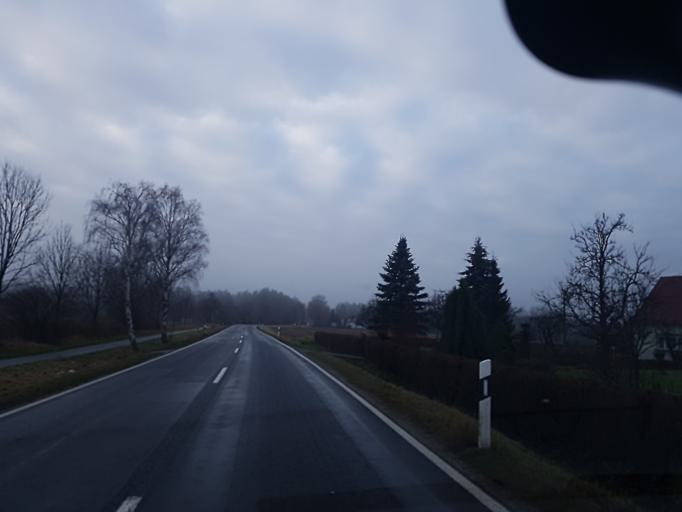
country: DE
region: Brandenburg
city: Finsterwalde
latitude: 51.6030
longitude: 13.7136
